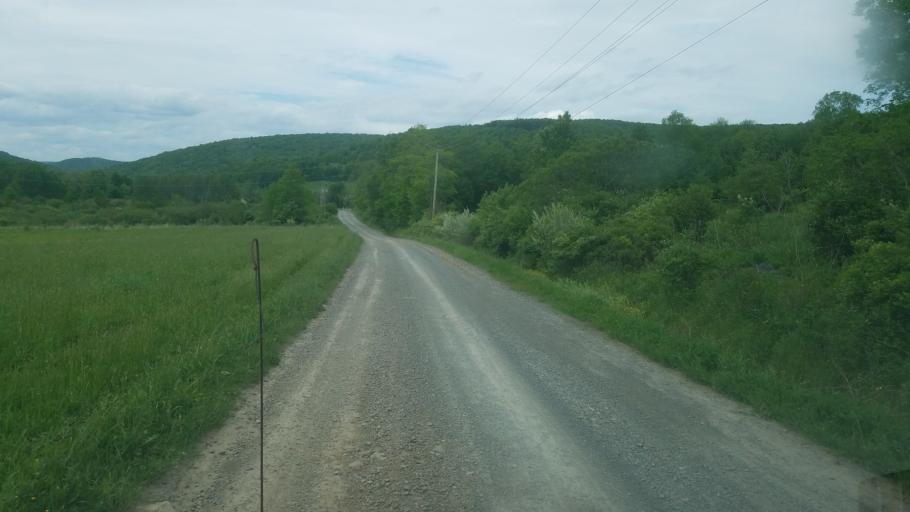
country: US
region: Pennsylvania
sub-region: Tioga County
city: Westfield
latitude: 41.8783
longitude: -77.5961
